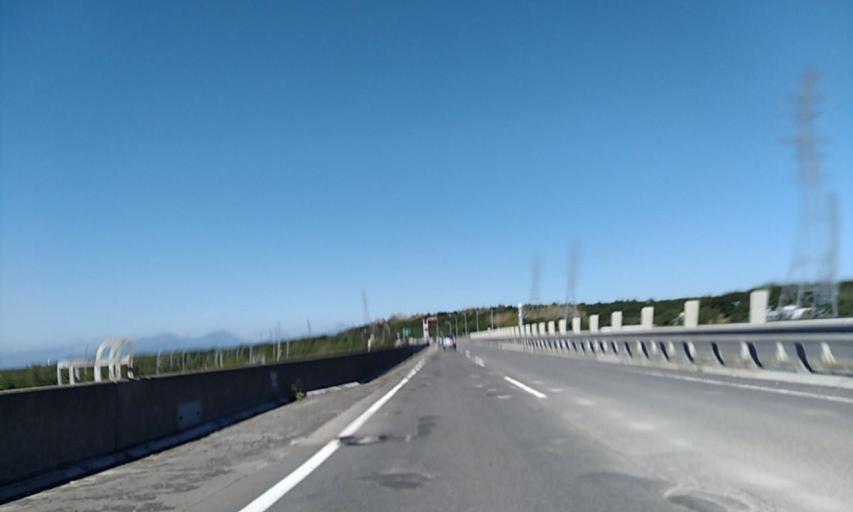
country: JP
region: Hokkaido
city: Tomakomai
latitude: 42.6710
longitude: 141.7901
